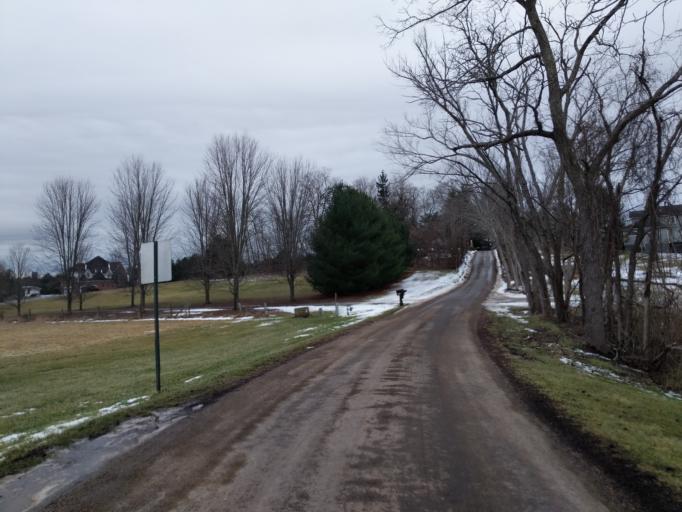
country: US
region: Ohio
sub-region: Athens County
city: The Plains
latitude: 39.3196
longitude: -82.1584
